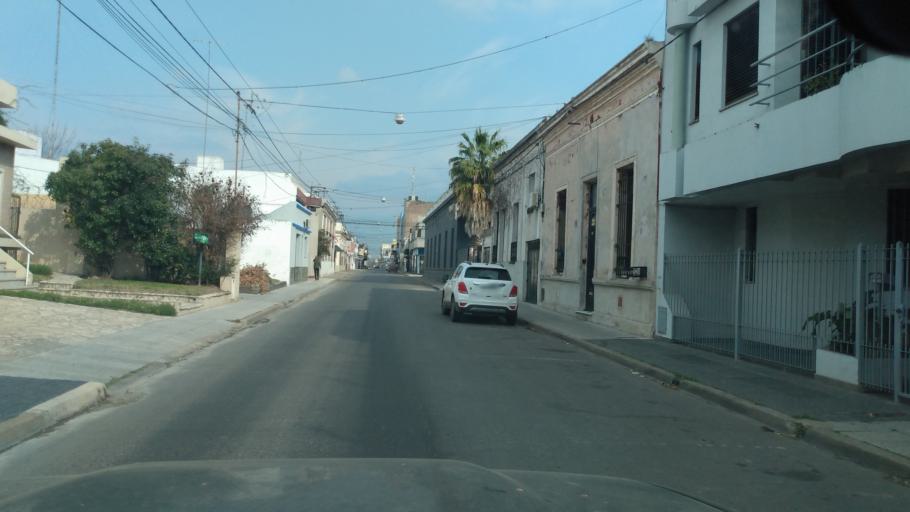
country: AR
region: Buenos Aires
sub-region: Partido de Lujan
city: Lujan
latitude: -34.5634
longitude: -59.1158
